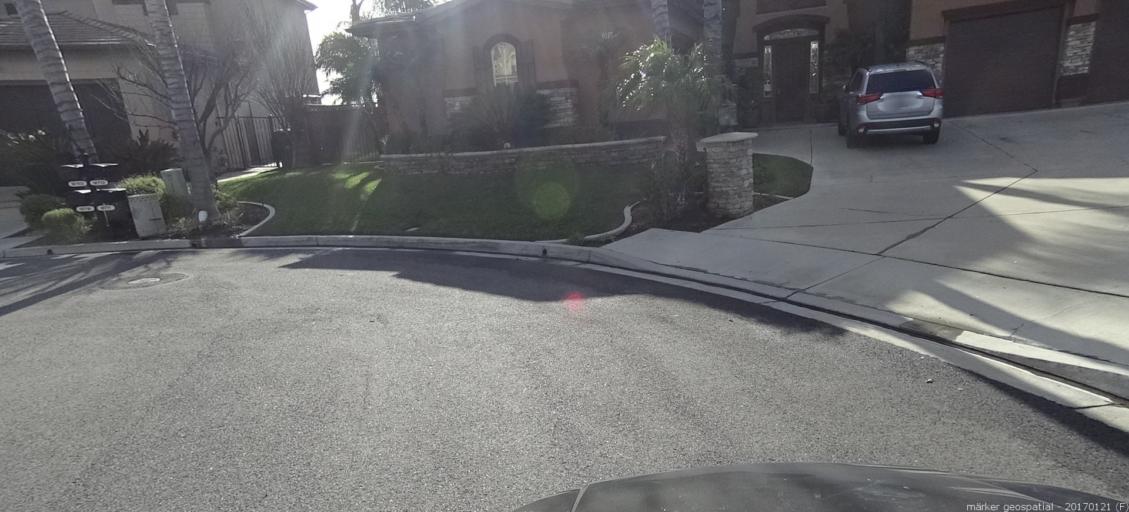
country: US
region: California
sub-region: Orange County
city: Portola Hills
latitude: 33.6903
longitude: -117.6193
